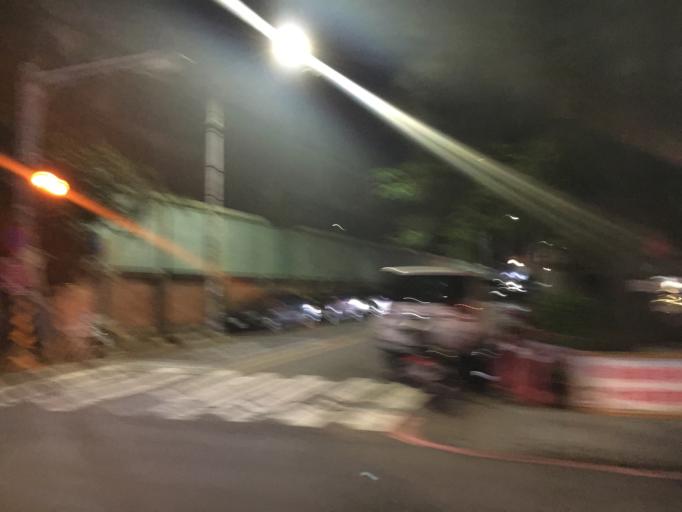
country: TW
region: Taiwan
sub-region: Hsinchu
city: Hsinchu
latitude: 24.7941
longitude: 120.9768
